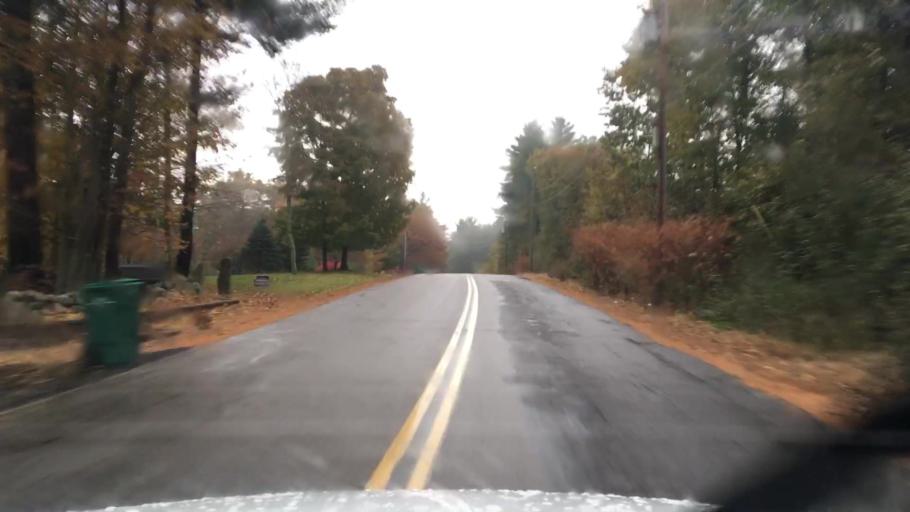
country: US
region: Maine
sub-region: York County
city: Berwick
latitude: 43.2740
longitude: -70.9105
